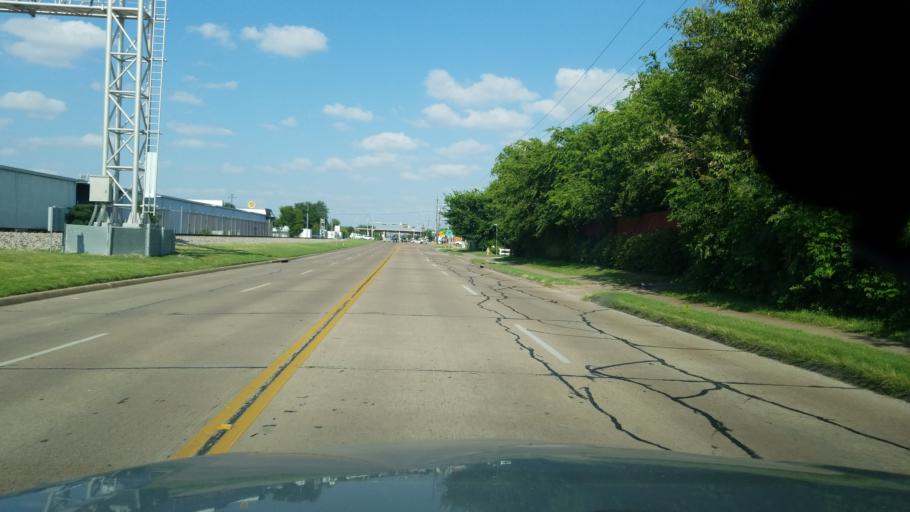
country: US
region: Texas
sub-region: Dallas County
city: Irving
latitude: 32.8151
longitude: -96.9661
